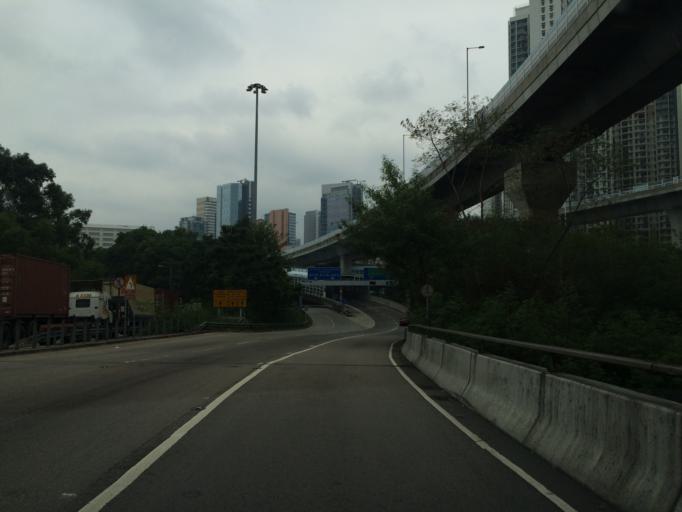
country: HK
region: Sham Shui Po
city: Sham Shui Po
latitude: 22.3315
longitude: 114.1434
